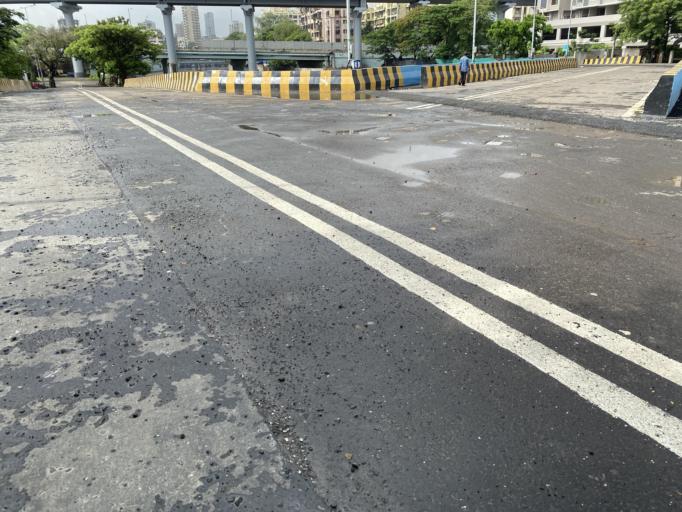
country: IN
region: Maharashtra
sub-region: Mumbai Suburban
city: Borivli
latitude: 19.2601
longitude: 72.8555
